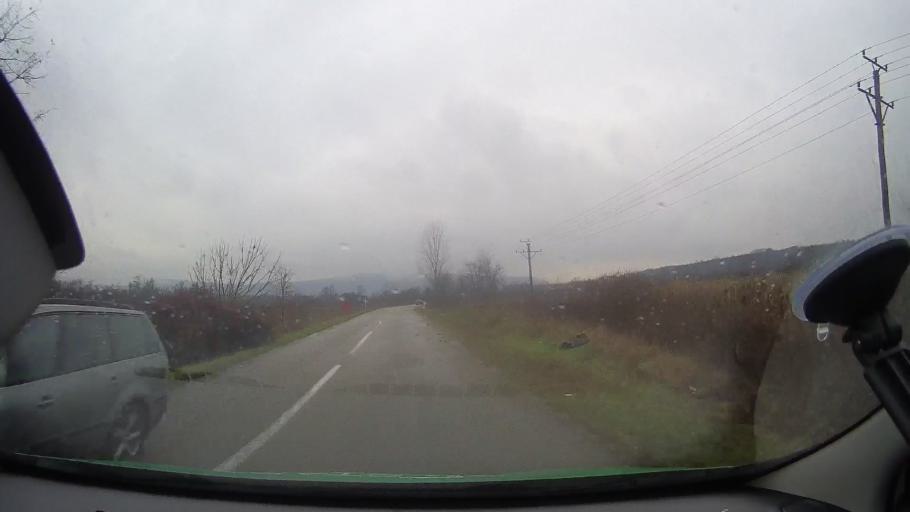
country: RO
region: Arad
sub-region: Comuna Ignesti
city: Ignesti
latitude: 46.3913
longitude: 22.1751
